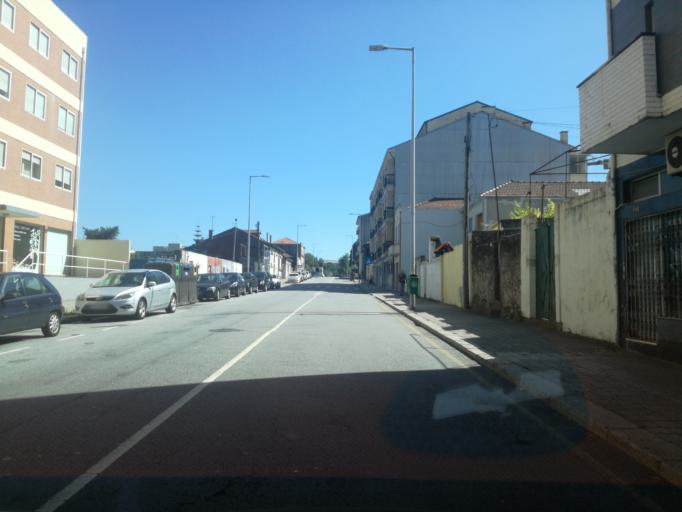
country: PT
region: Porto
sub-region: Matosinhos
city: Sao Mamede de Infesta
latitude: 41.1829
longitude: -8.6095
